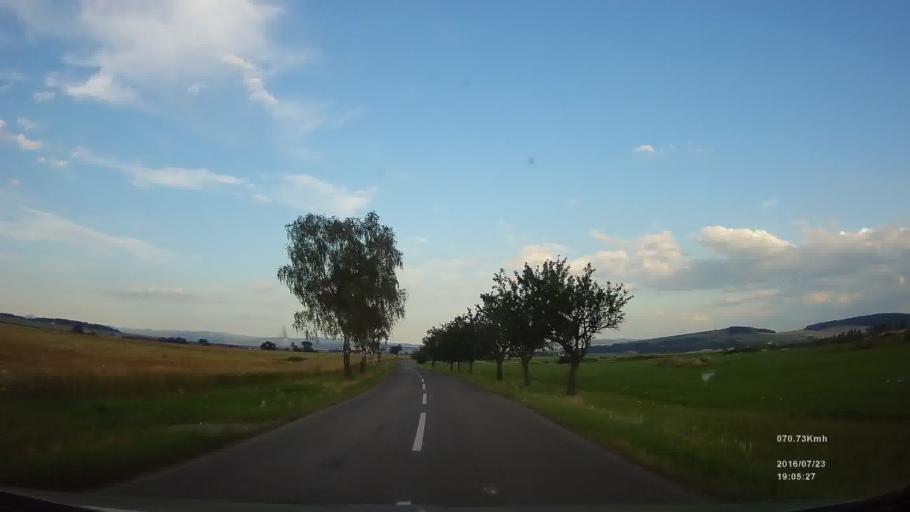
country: SK
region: Presovsky
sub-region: Okres Poprad
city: Nova Lesna
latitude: 49.1283
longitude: 20.3250
